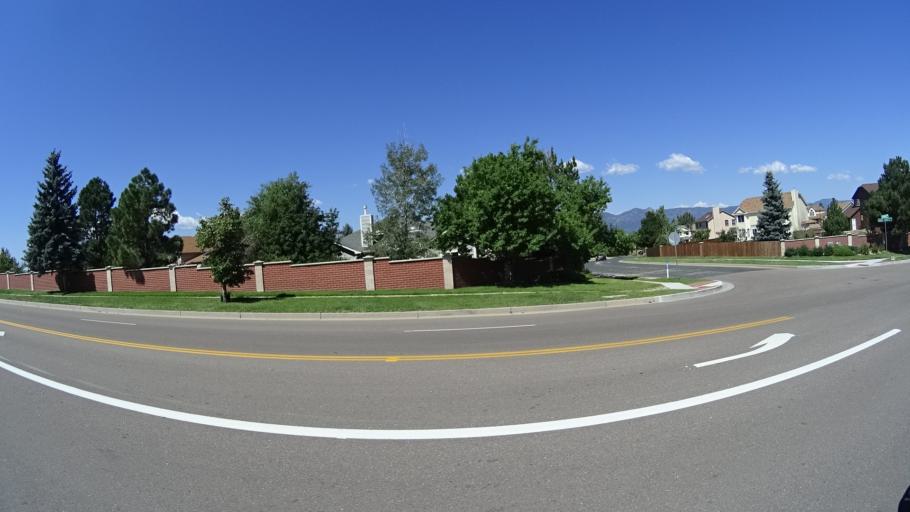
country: US
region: Colorado
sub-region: El Paso County
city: Black Forest
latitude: 38.9590
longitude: -104.7696
